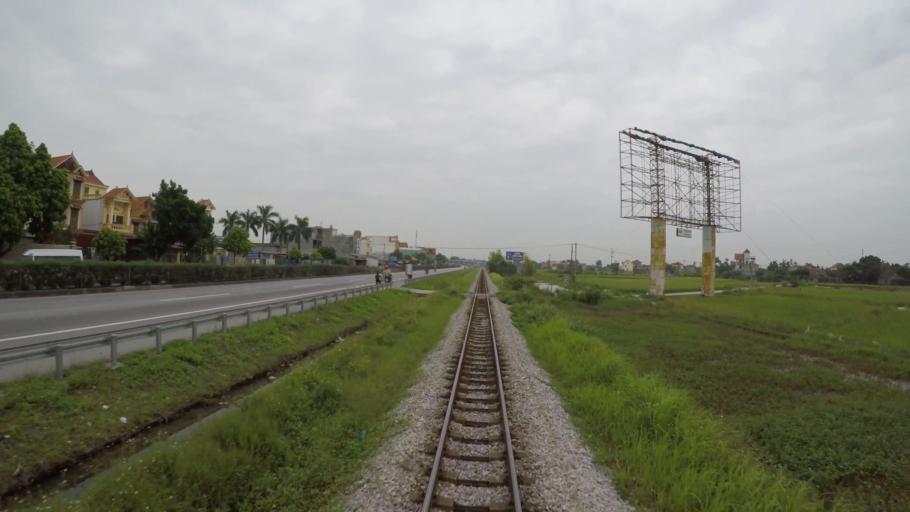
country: VN
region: Hai Duong
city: Phu Thai
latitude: 20.9294
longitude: 106.5546
